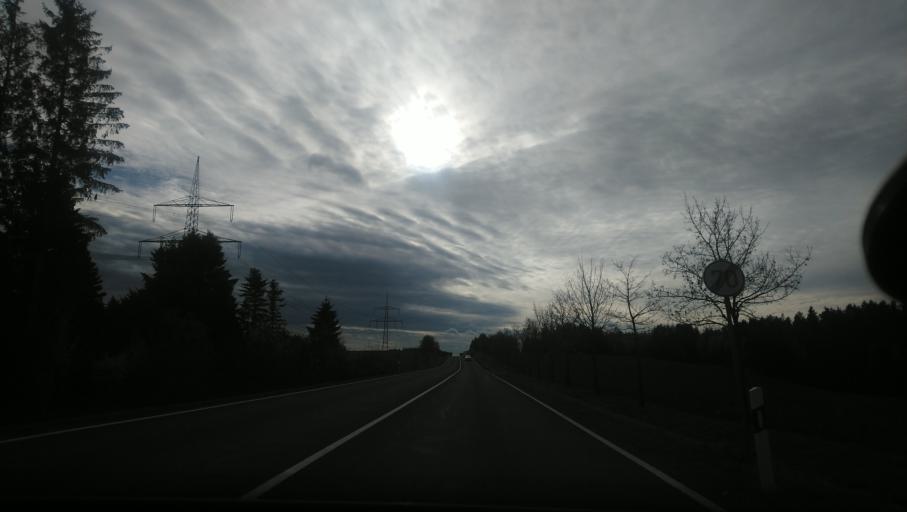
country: DE
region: Saxony
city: Stollberg
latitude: 50.6913
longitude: 12.7990
